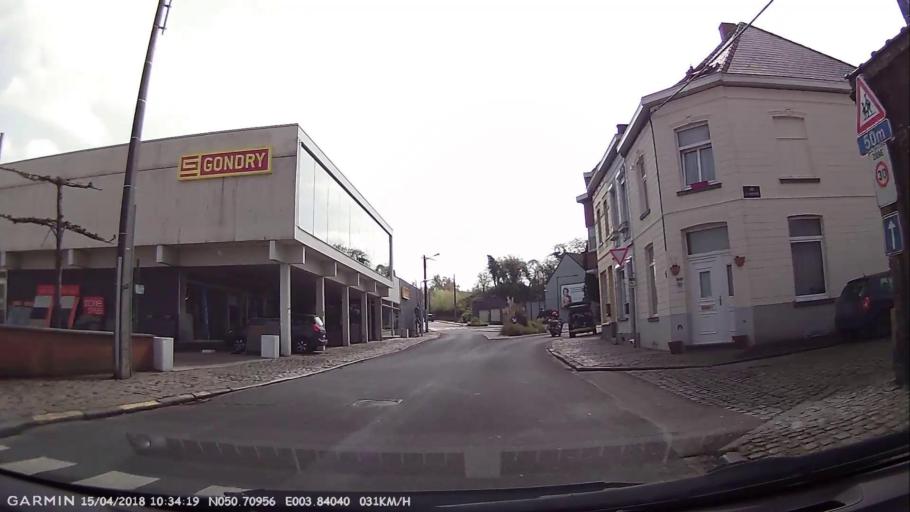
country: BE
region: Wallonia
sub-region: Province du Hainaut
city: Lessines
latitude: 50.7096
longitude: 3.8405
